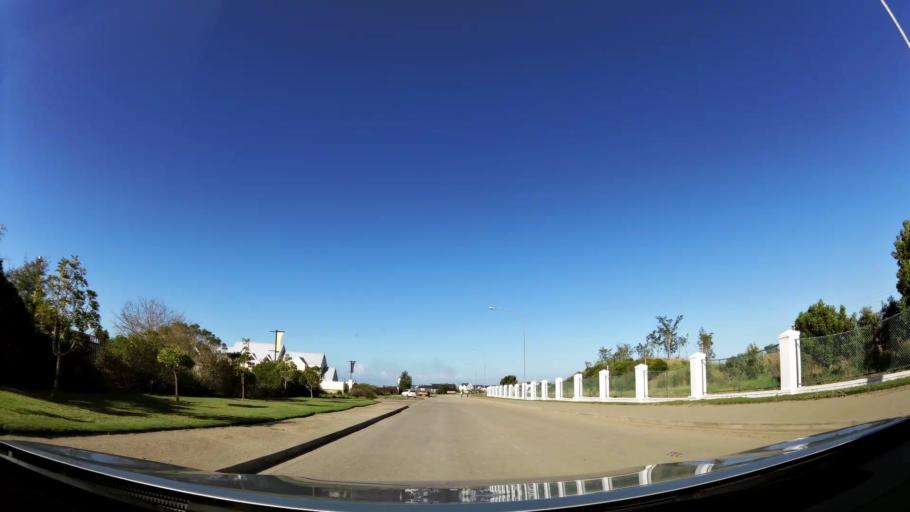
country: ZA
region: Western Cape
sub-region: Eden District Municipality
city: George
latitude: -33.9676
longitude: 22.4291
